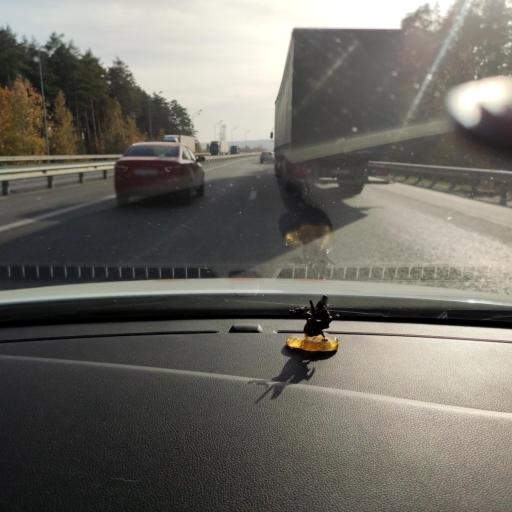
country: RU
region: Tatarstan
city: Osinovo
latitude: 55.8278
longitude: 48.8483
